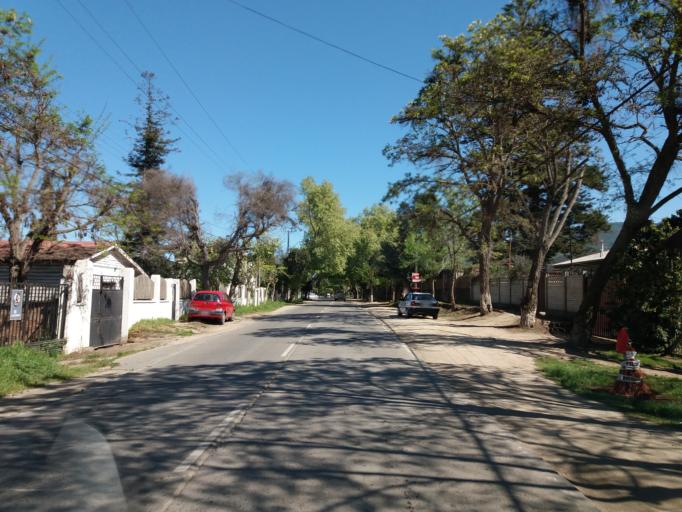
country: CL
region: Valparaiso
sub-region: Provincia de Marga Marga
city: Limache
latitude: -32.9997
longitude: -71.2128
